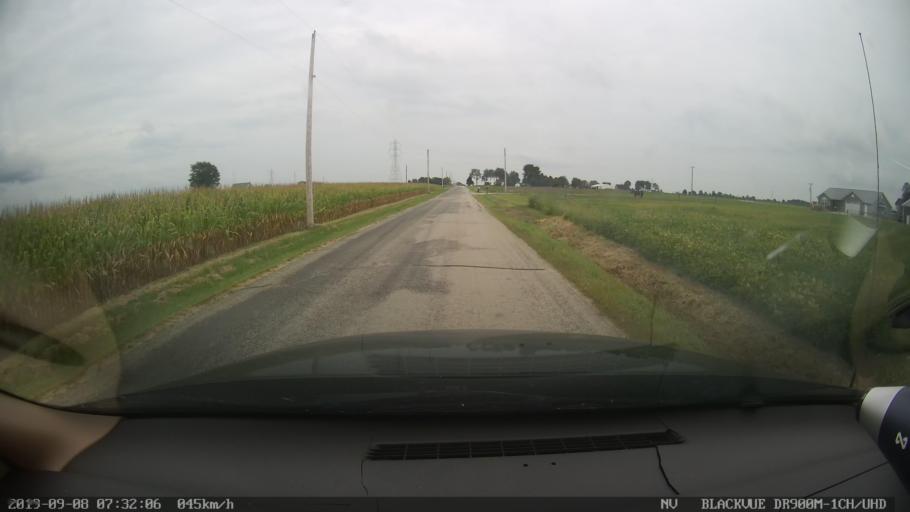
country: US
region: Ohio
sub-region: Richland County
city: Shelby
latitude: 40.8634
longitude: -82.6958
